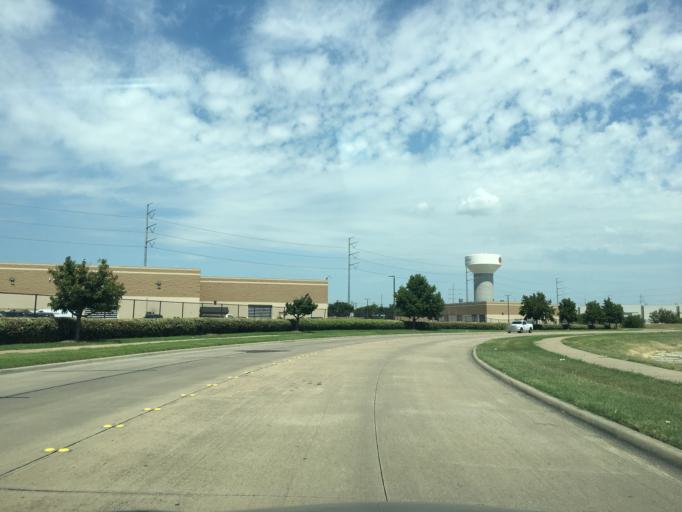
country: US
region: Texas
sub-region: Dallas County
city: Garland
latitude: 32.8667
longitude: -96.6601
